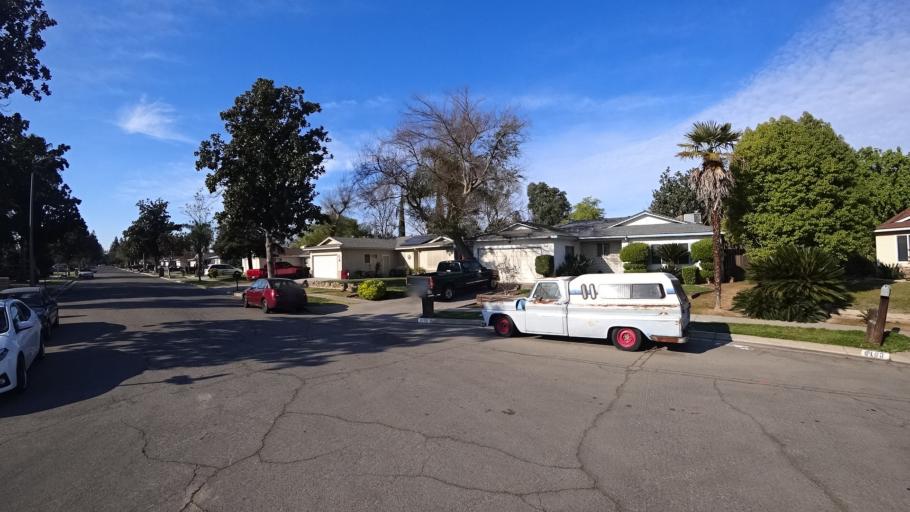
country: US
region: California
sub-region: Fresno County
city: Fresno
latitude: 36.8256
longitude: -119.8570
